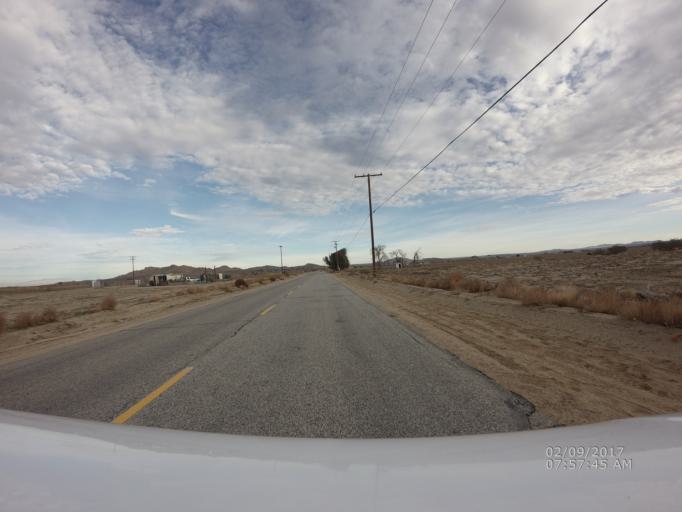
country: US
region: California
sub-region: Los Angeles County
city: Lake Los Angeles
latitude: 34.5644
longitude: -117.8356
